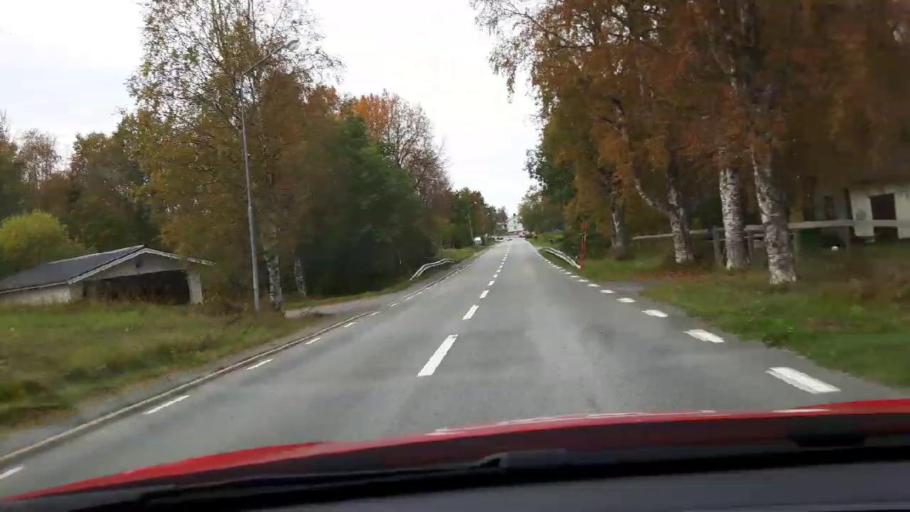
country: SE
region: Jaemtland
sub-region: Krokoms Kommun
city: Krokom
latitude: 63.1725
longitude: 14.1015
